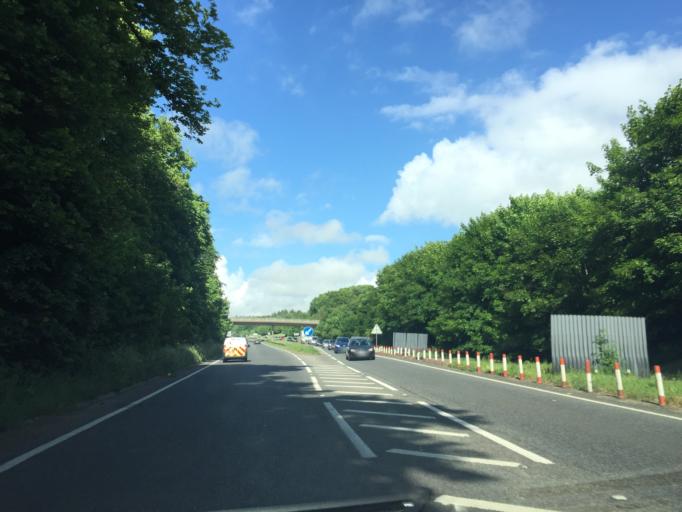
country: GB
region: England
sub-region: Dorset
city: Dorchester
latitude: 50.7344
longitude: -2.3947
